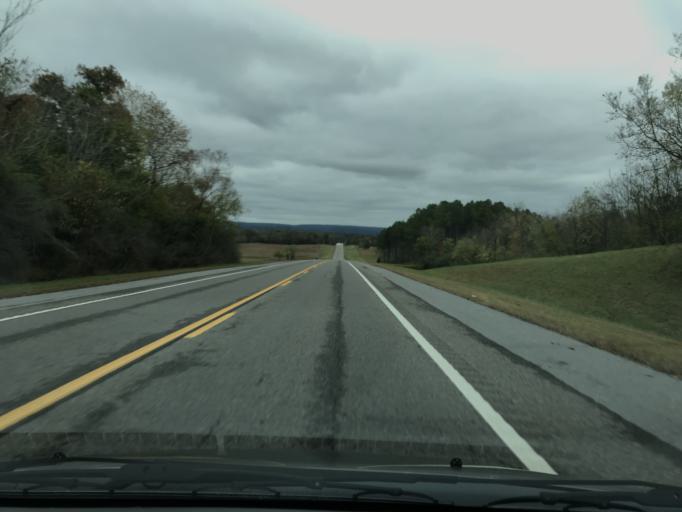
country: US
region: Tennessee
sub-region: Rhea County
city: Graysville
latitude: 35.3968
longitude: -85.0108
